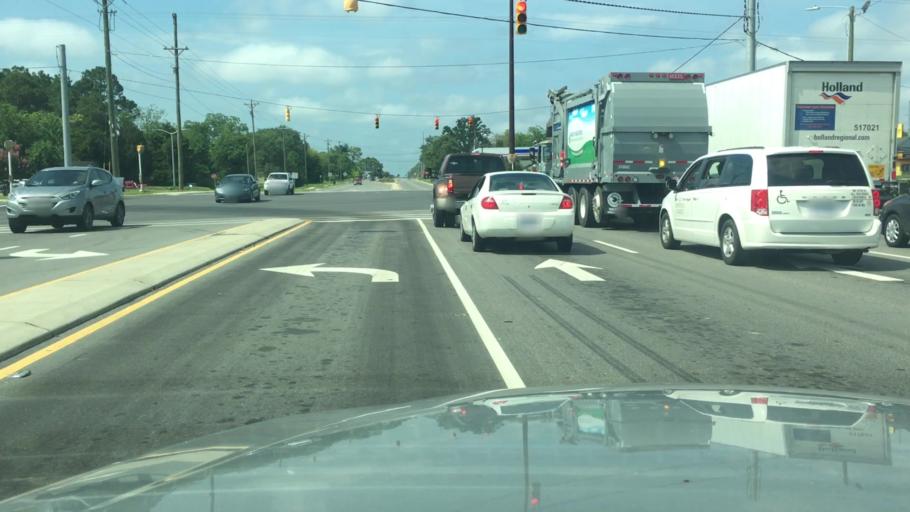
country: US
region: North Carolina
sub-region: Cumberland County
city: Fayetteville
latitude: 35.0186
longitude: -78.9039
